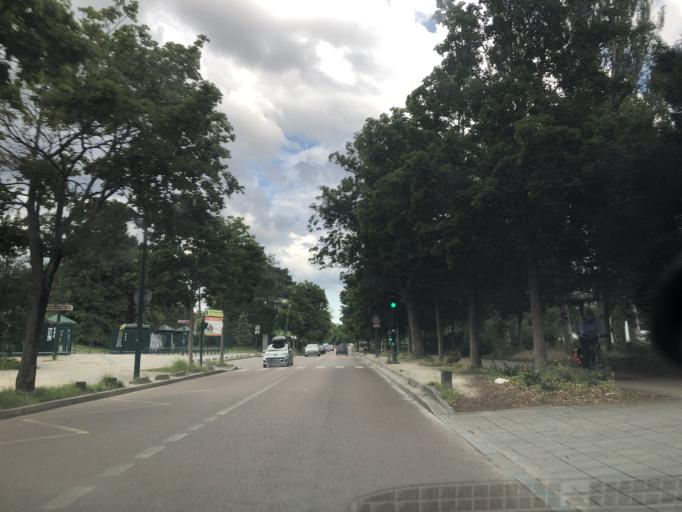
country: FR
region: Ile-de-France
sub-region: Departement du Val-de-Marne
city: Vincennes
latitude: 48.8372
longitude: 2.4407
